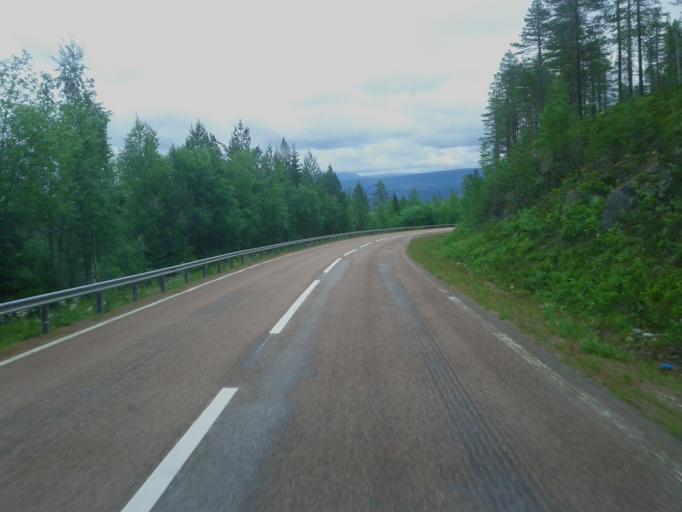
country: NO
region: Hedmark
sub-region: Trysil
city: Innbygda
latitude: 61.8494
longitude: 12.6085
